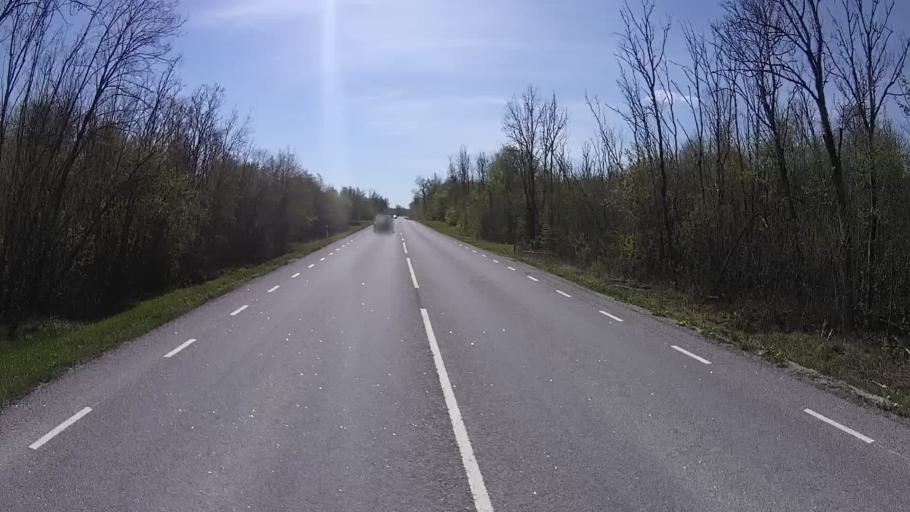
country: EE
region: Laeaene
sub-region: Ridala Parish
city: Uuemoisa
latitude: 58.9731
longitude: 23.6773
